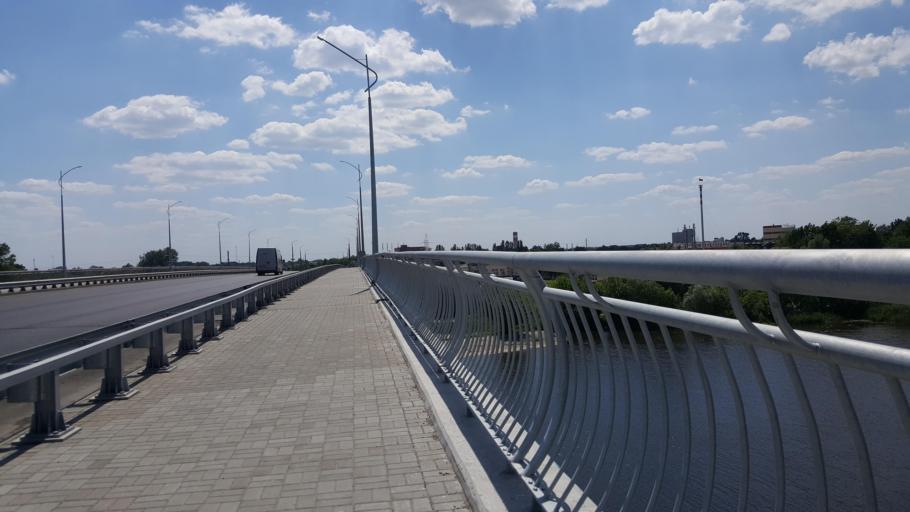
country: BY
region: Brest
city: Kobryn
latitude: 52.2149
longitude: 24.3319
